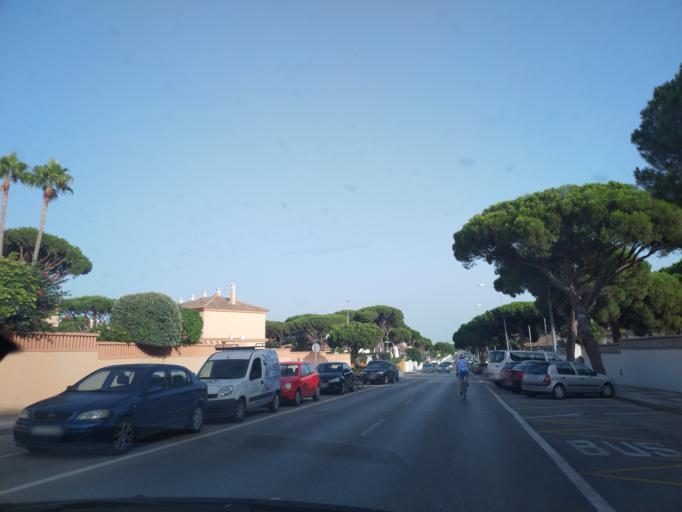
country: ES
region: Andalusia
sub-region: Provincia de Cadiz
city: Chiclana de la Frontera
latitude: 36.3764
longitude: -6.1866
